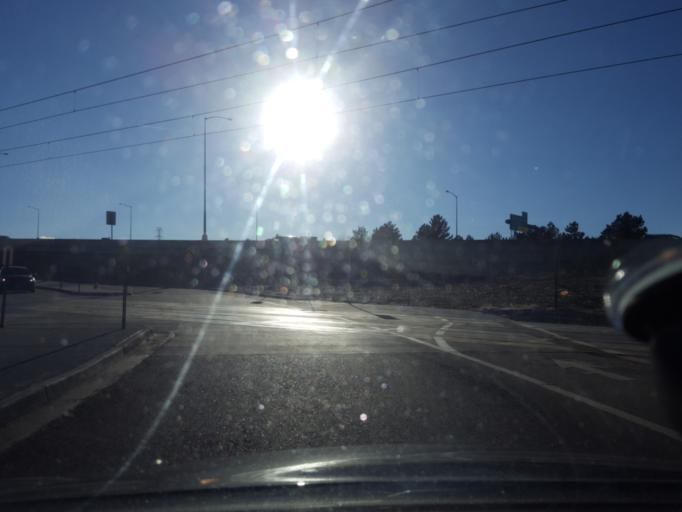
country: US
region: Colorado
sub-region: Adams County
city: Aurora
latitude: 39.7220
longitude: -104.8247
